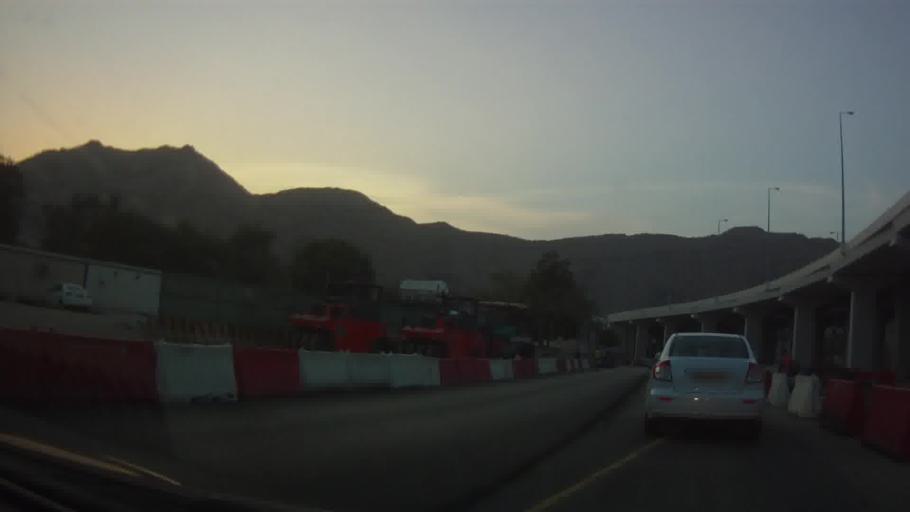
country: OM
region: Muhafazat Masqat
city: Muscat
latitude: 23.6187
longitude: 58.5410
